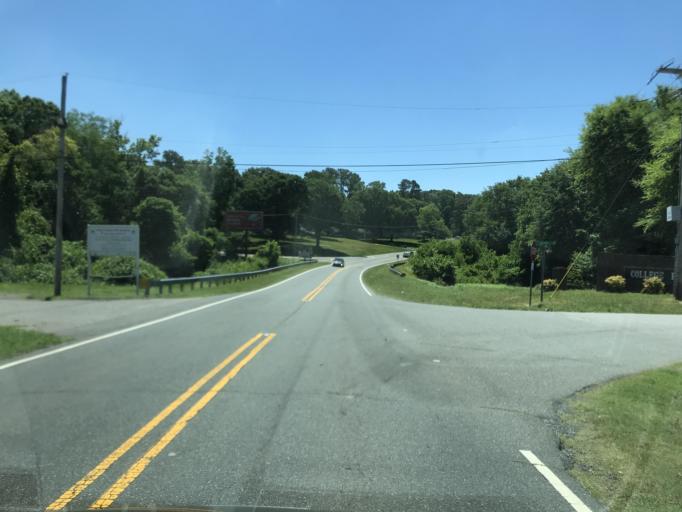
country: US
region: North Carolina
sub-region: Gaston County
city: Dallas
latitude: 35.3243
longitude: -81.1938
